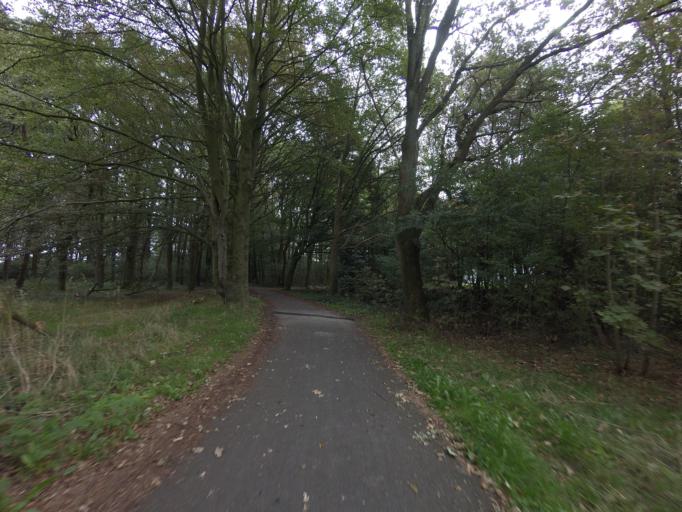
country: NL
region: Drenthe
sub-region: Gemeente Assen
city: Assen
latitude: 52.9107
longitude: 6.5188
